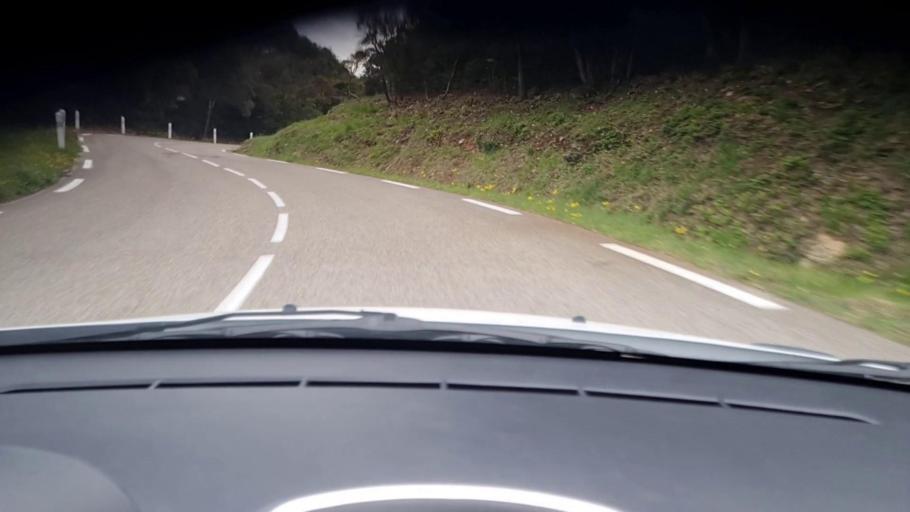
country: FR
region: Languedoc-Roussillon
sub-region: Departement du Gard
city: Poulx
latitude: 43.9273
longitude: 4.3907
